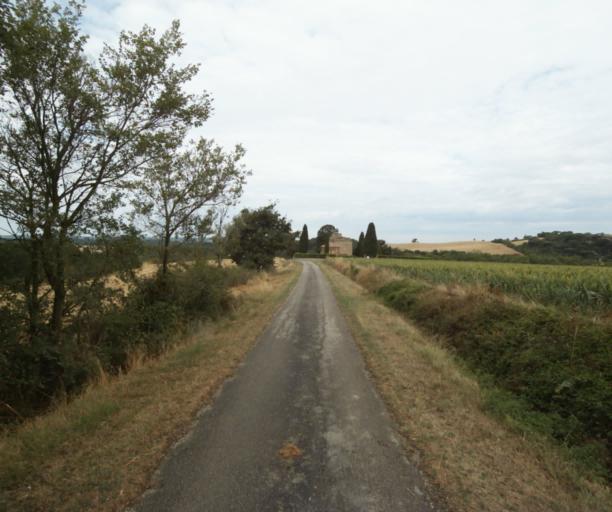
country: FR
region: Midi-Pyrenees
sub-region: Departement de la Haute-Garonne
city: Revel
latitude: 43.4223
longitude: 1.9828
